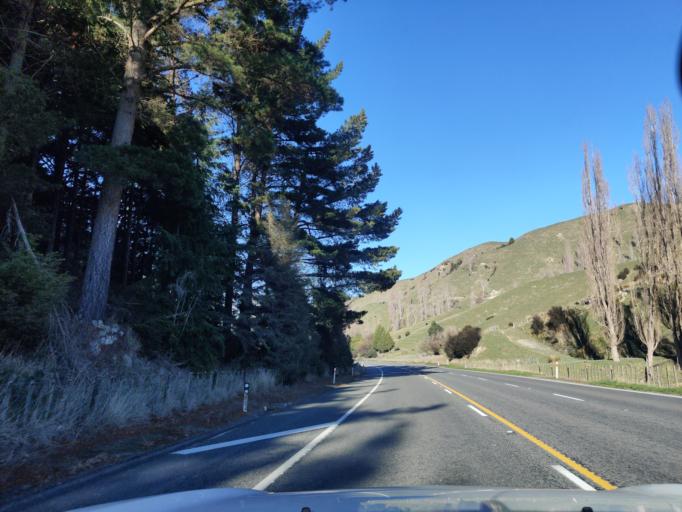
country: NZ
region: Manawatu-Wanganui
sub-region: Ruapehu District
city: Waiouru
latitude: -39.7758
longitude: 175.7895
